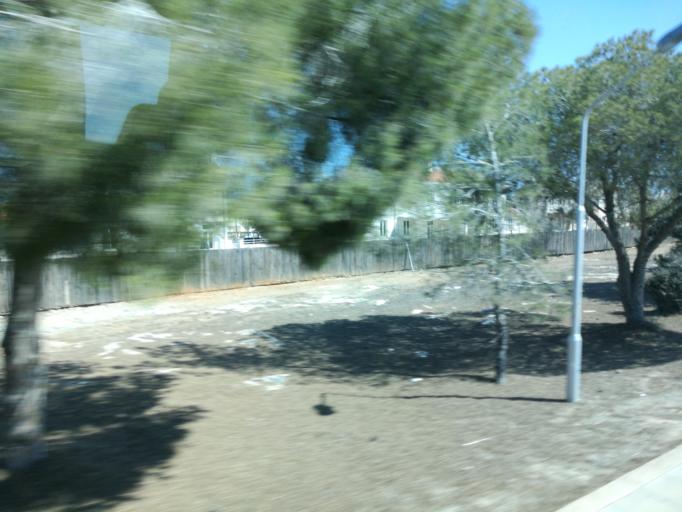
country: CY
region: Ammochostos
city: Acheritou
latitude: 35.0870
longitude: 33.8857
